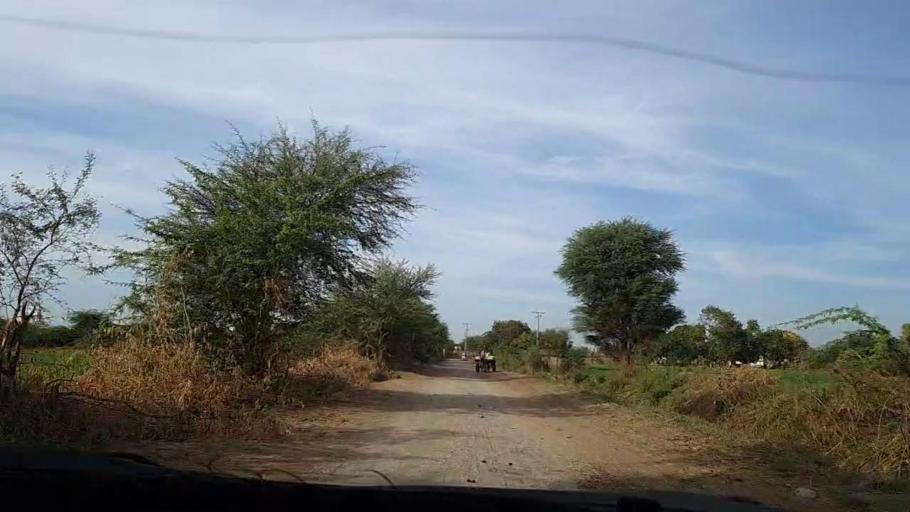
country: PK
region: Sindh
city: Dhoro Naro
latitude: 25.4479
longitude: 69.5126
